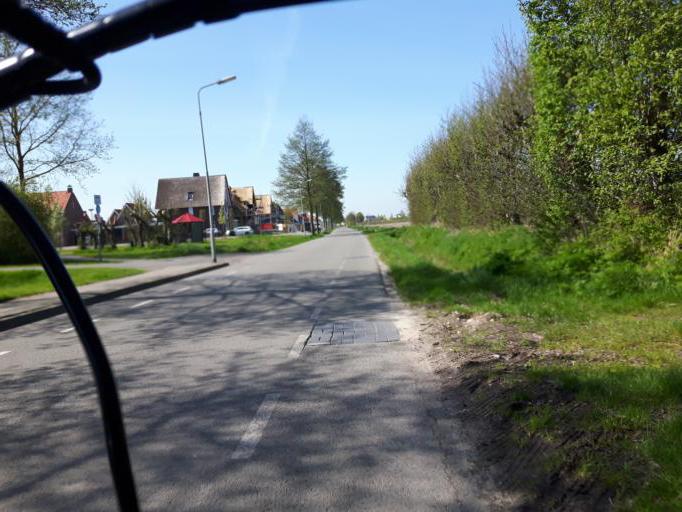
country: NL
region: Zeeland
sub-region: Gemeente Goes
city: Goes
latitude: 51.4779
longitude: 3.9570
